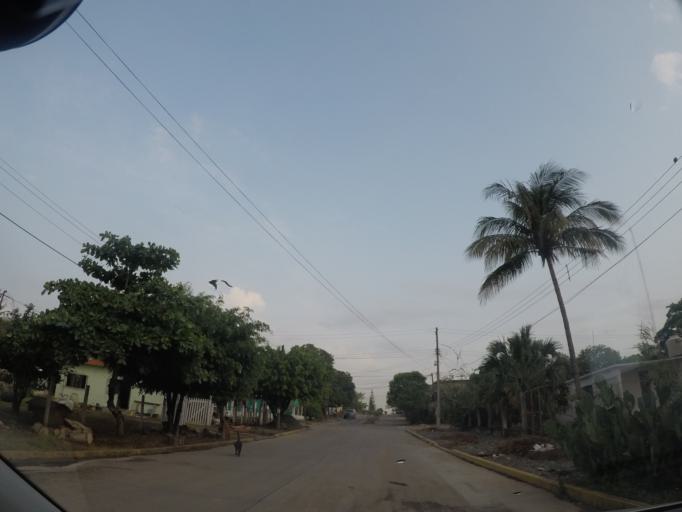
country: MX
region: Oaxaca
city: Matias Romero
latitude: 16.8714
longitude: -95.0369
